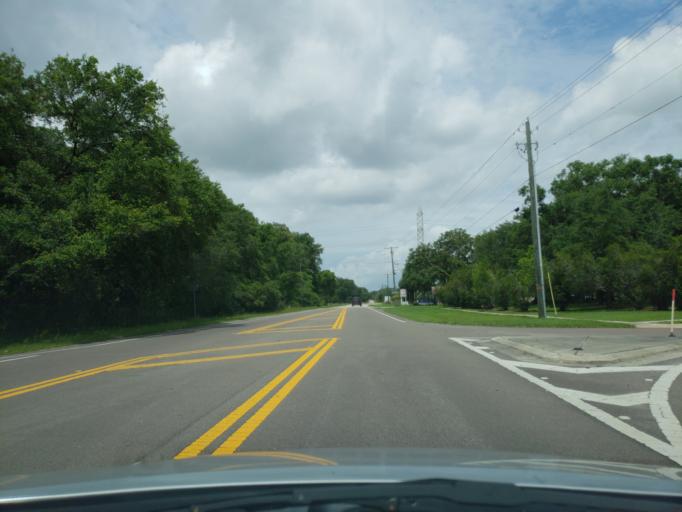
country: US
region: Florida
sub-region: Hillsborough County
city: East Lake-Orient Park
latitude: 28.0110
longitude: -82.3587
